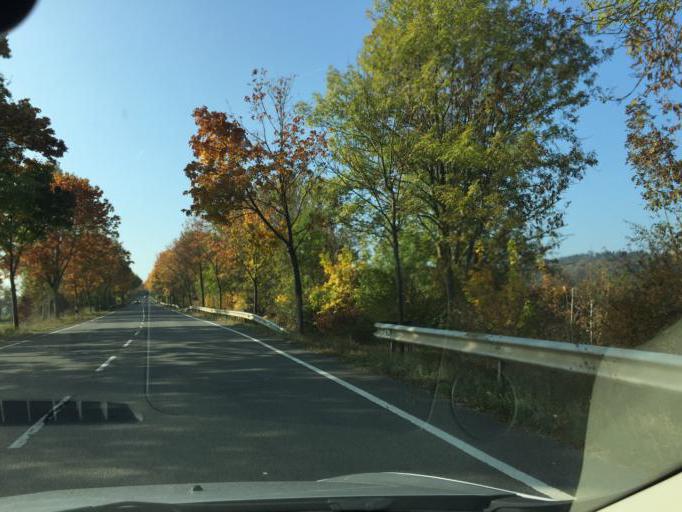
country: LU
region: Grevenmacher
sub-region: Canton de Remich
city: Bous
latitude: 49.5461
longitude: 6.3121
